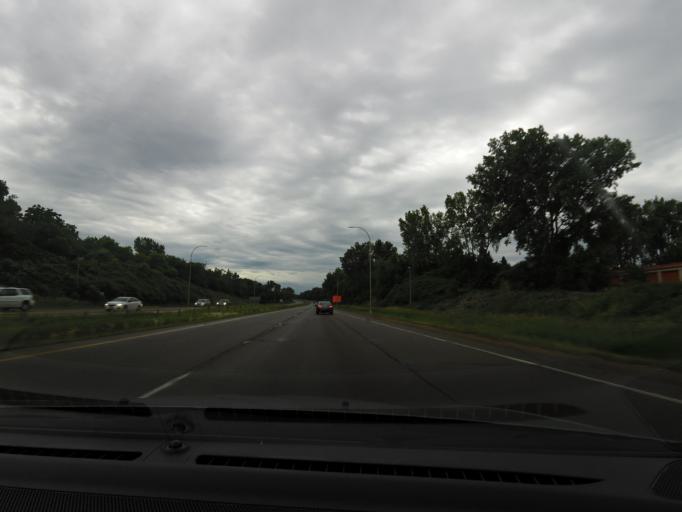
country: US
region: Minnesota
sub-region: Dakota County
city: South Saint Paul
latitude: 44.8937
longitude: -93.0665
